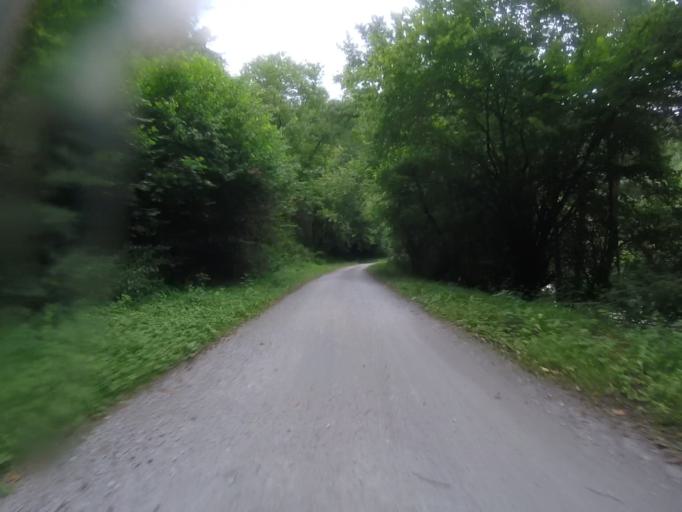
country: ES
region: Navarre
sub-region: Provincia de Navarra
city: Sunbilla
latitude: 43.1999
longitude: -1.6732
